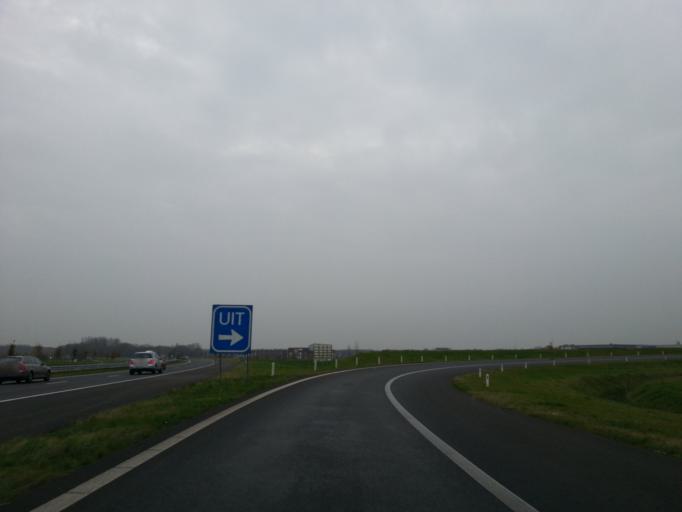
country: NL
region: North Brabant
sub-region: Gemeente Bergen op Zoom
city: Lepelstraat
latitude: 51.5428
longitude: 4.2935
